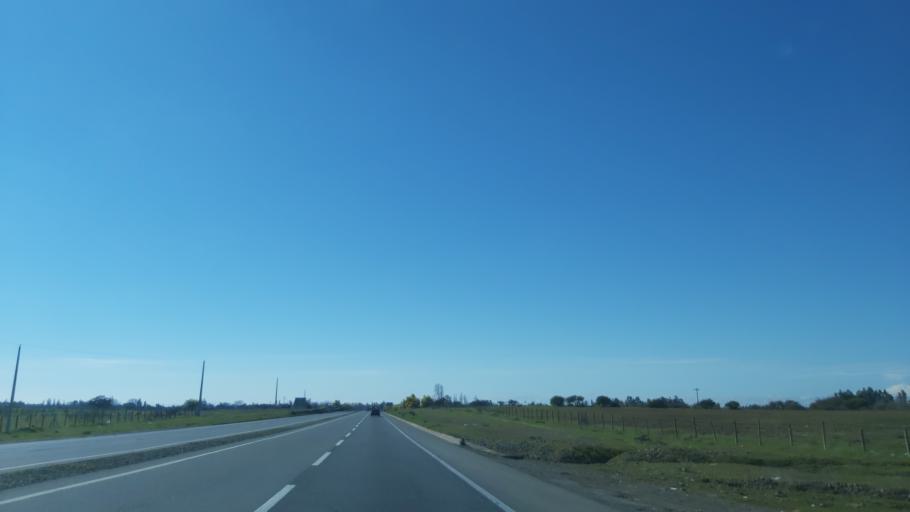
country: CL
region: Biobio
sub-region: Provincia de Nuble
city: Bulnes
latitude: -36.6570
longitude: -72.2470
